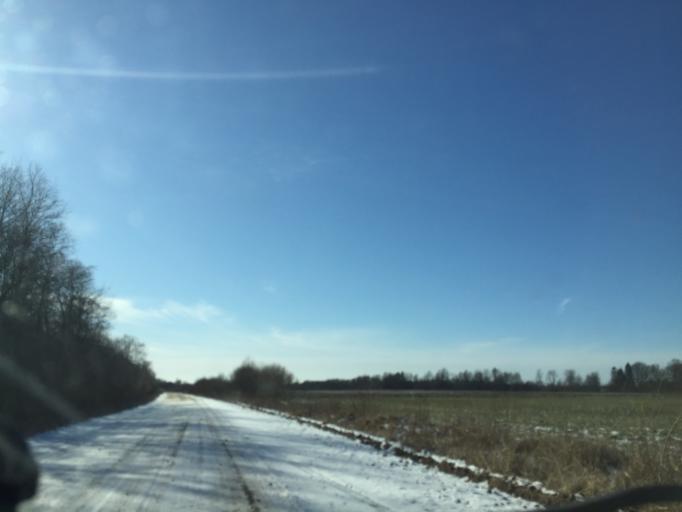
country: LV
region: Ventspils Rajons
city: Piltene
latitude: 57.2667
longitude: 21.6734
